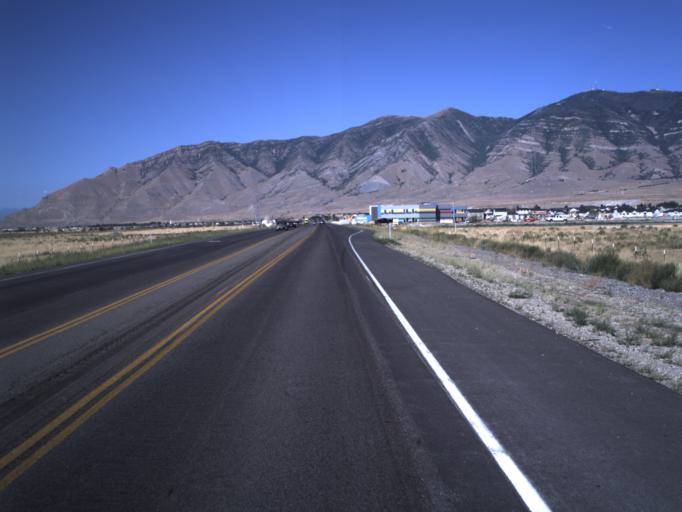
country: US
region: Utah
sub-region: Tooele County
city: Stansbury park
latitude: 40.6362
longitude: -112.3280
